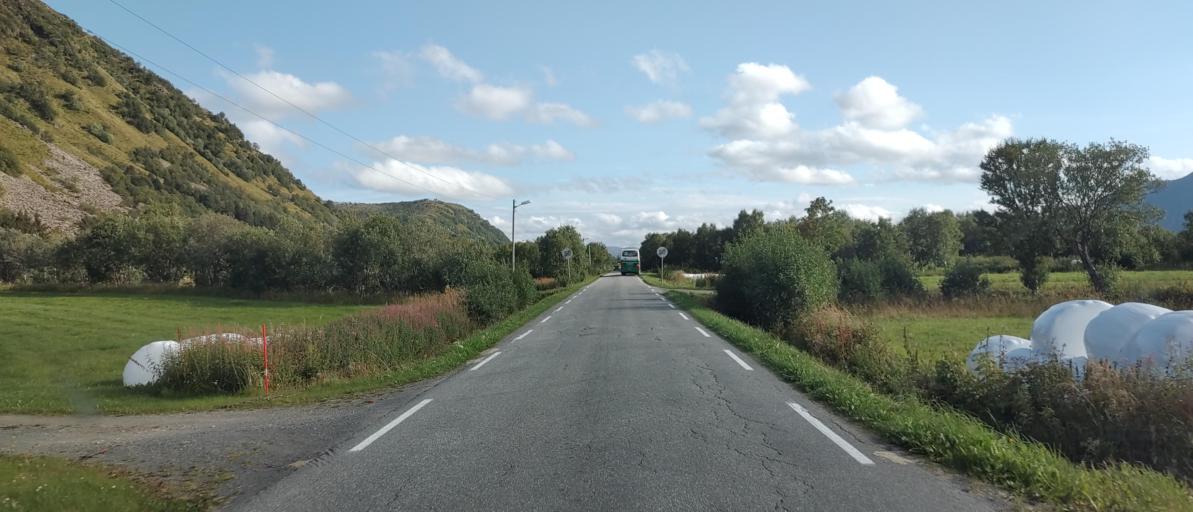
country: NO
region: Nordland
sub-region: Sortland
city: Sortland
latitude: 69.0367
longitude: 15.5213
